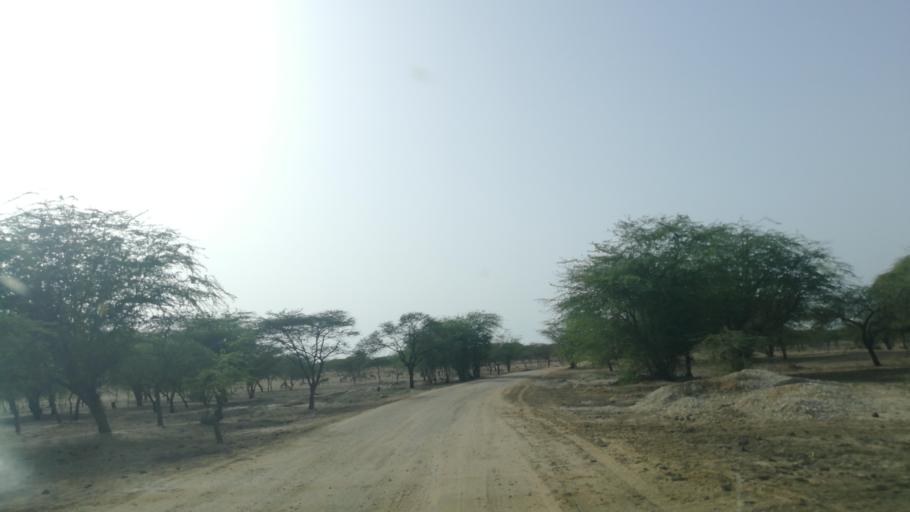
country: SN
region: Saint-Louis
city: Saint-Louis
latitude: 16.0615
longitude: -16.3342
